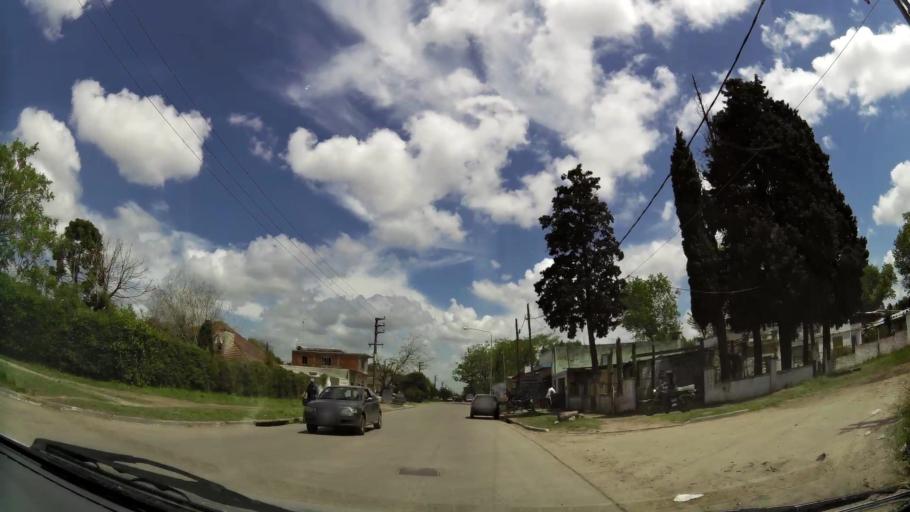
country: AR
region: Buenos Aires
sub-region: Partido de Quilmes
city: Quilmes
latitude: -34.8129
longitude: -58.2323
